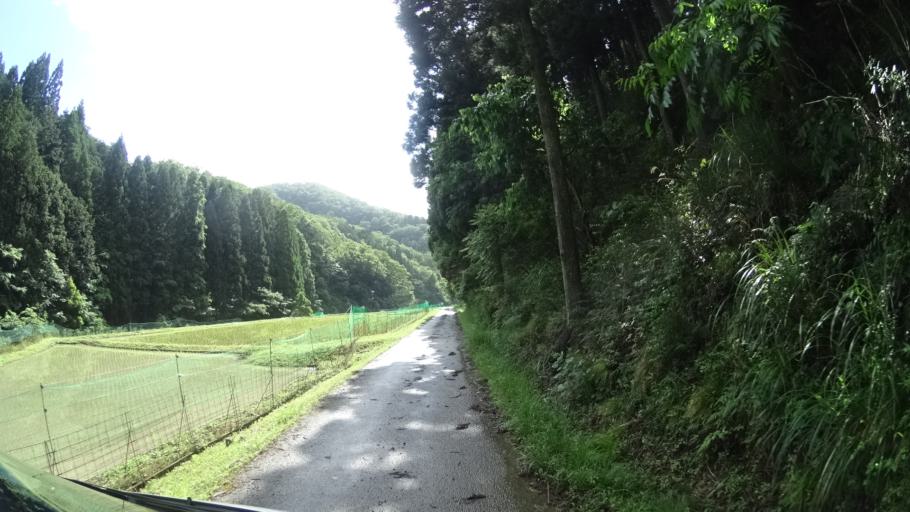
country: JP
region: Kyoto
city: Maizuru
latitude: 35.3902
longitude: 135.2745
